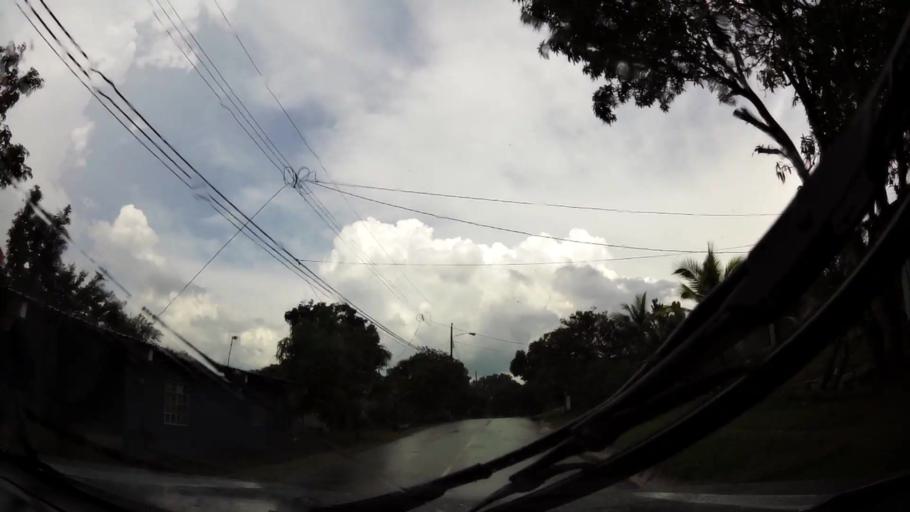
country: PA
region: Panama
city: Cabra Numero Uno
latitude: 9.1037
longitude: -79.3359
